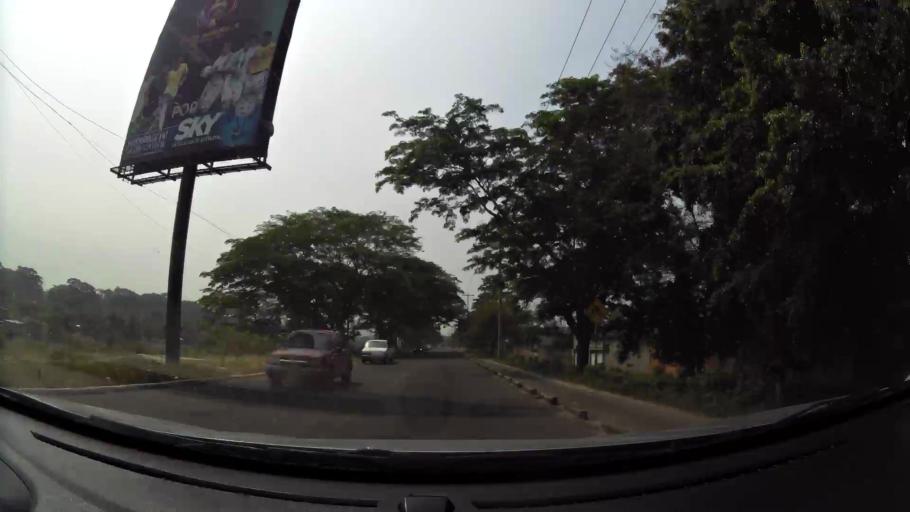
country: HN
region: Cortes
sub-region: San Pedro Sula
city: Pena Blanca
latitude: 15.5595
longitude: -88.0179
